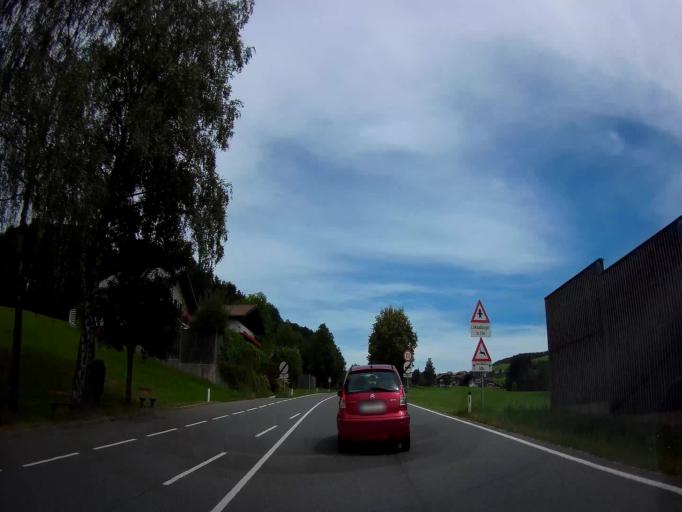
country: AT
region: Salzburg
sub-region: Politischer Bezirk Salzburg-Umgebung
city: Hallwang
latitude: 47.8413
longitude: 13.0924
